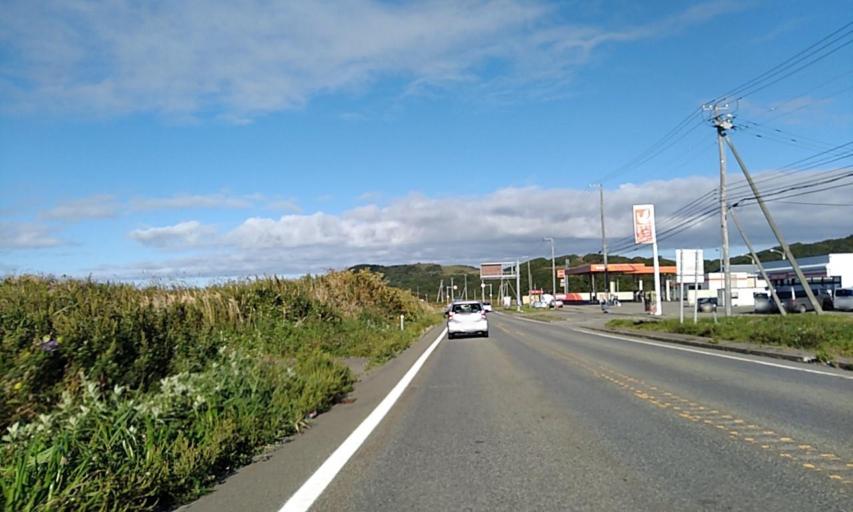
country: JP
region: Hokkaido
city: Shizunai-furukawacho
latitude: 42.1846
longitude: 142.7244
